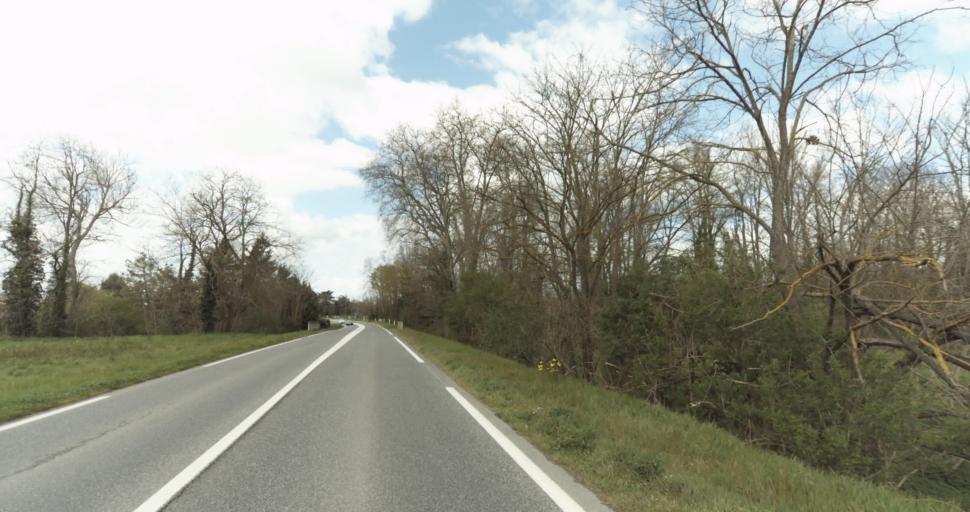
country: FR
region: Midi-Pyrenees
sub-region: Departement de la Haute-Garonne
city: Auterive
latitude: 43.3338
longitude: 1.4859
